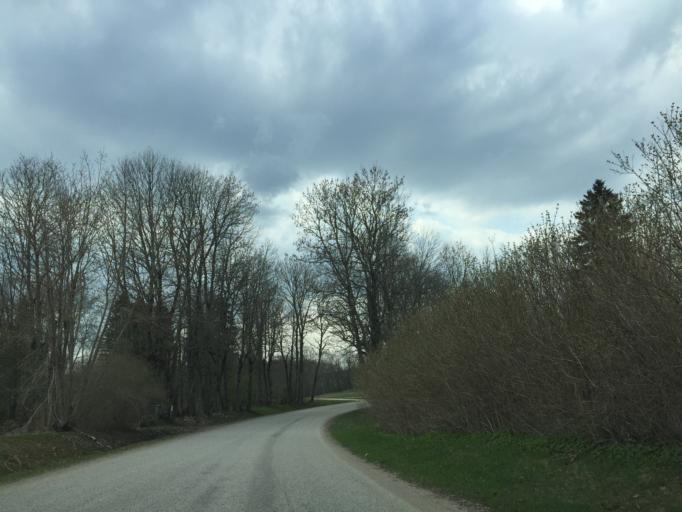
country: RU
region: Pskov
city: Pechory
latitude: 57.7278
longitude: 27.3582
